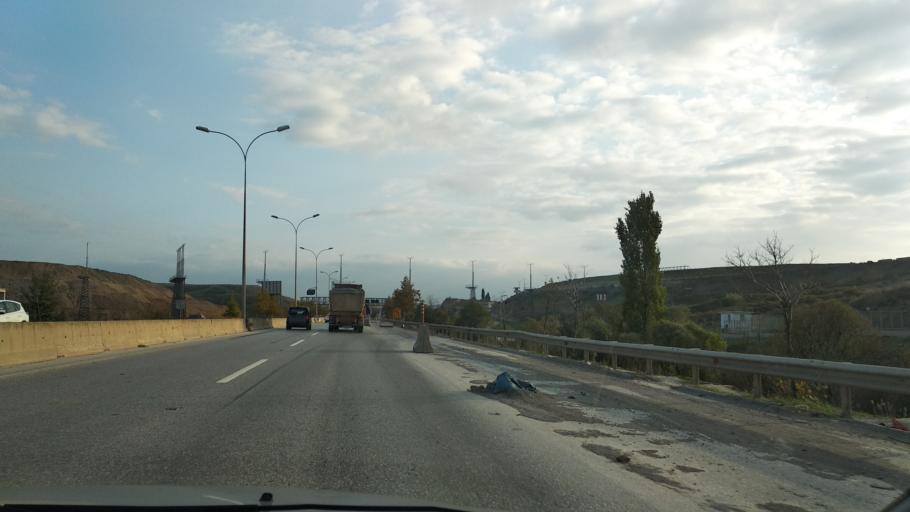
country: TR
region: Istanbul
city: Pendik
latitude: 40.9079
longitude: 29.3272
